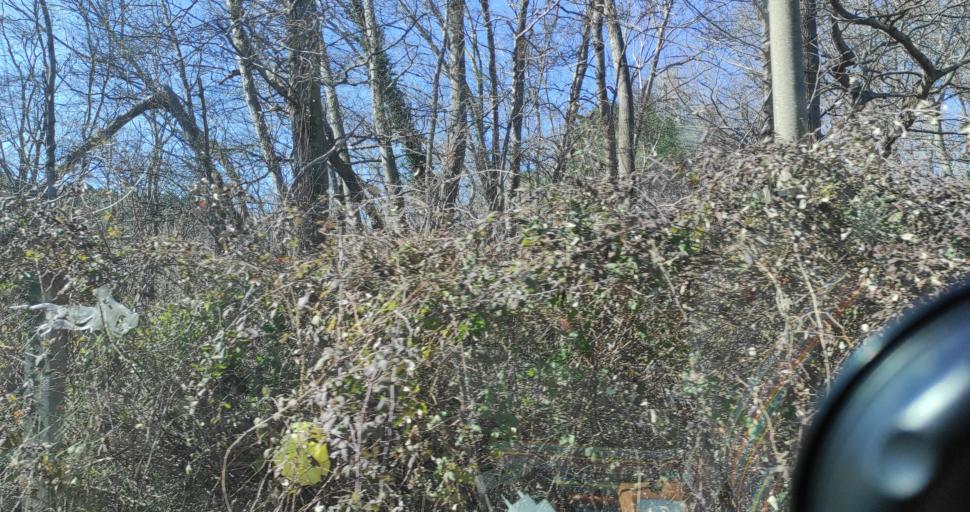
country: AL
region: Shkoder
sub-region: Rrethi i Shkodres
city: Velipoje
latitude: 41.8655
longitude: 19.4062
